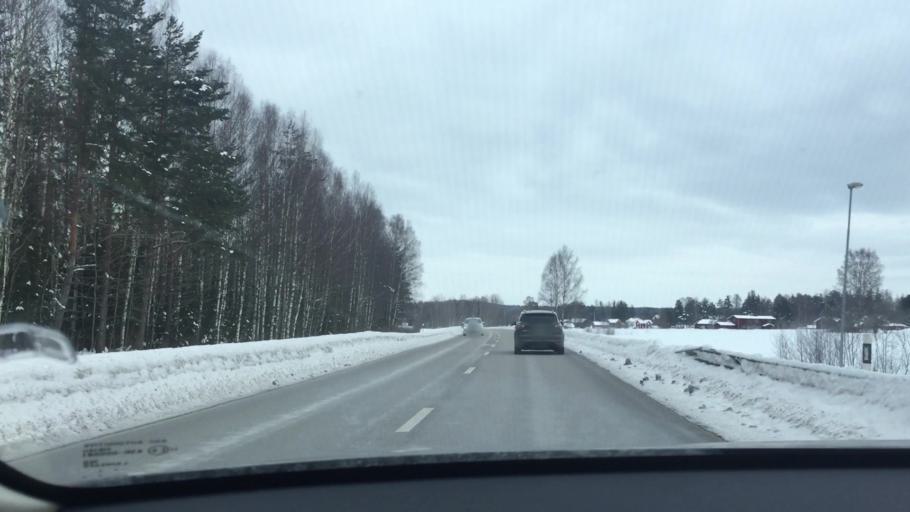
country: SE
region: Dalarna
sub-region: Faluns Kommun
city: Svardsjo
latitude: 60.6402
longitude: 15.8402
